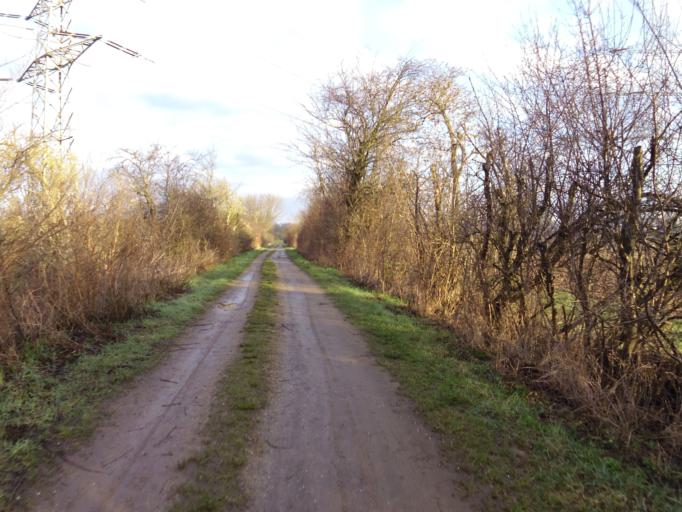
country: DE
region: Rheinland-Pfalz
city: Bobenheim-Roxheim
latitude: 49.6024
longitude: 8.4016
